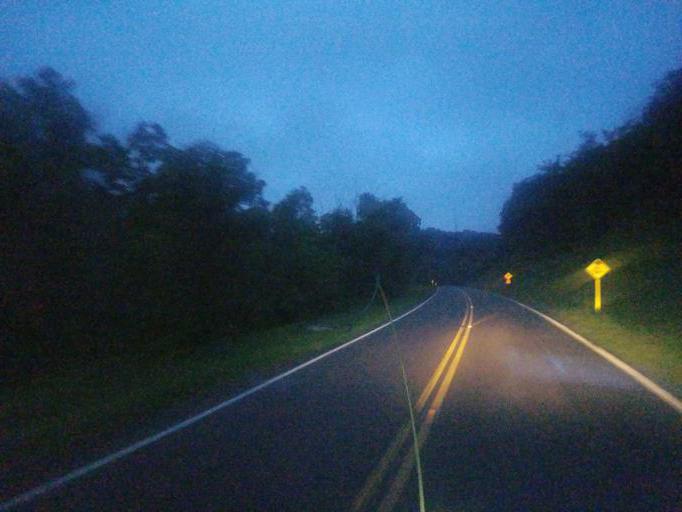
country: US
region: Ohio
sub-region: Carroll County
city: Carrollton
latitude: 40.5848
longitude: -81.0295
